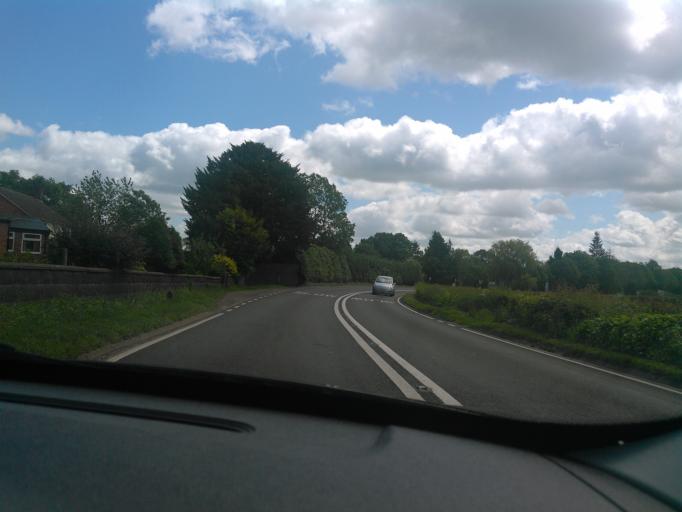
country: GB
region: England
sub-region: Shropshire
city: Prees
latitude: 52.8817
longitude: -2.6574
